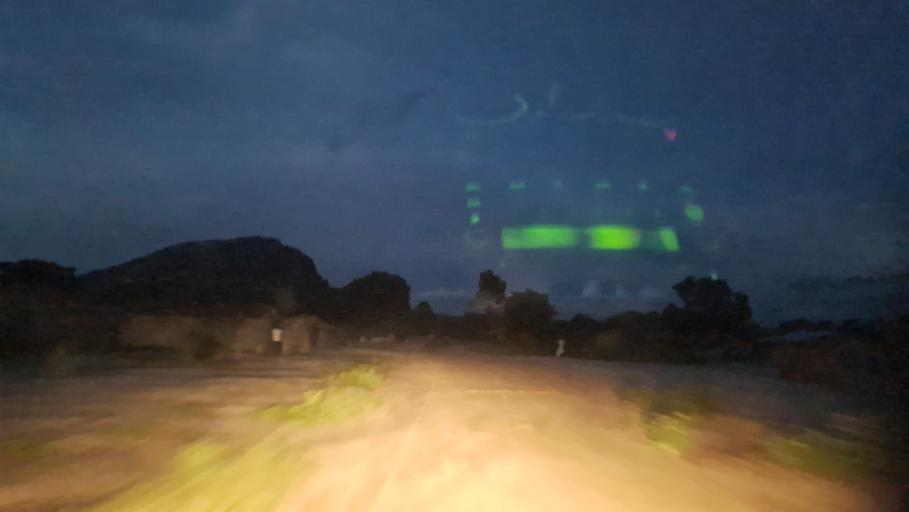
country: MZ
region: Nampula
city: Nampula
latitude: -14.6653
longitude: 39.8369
